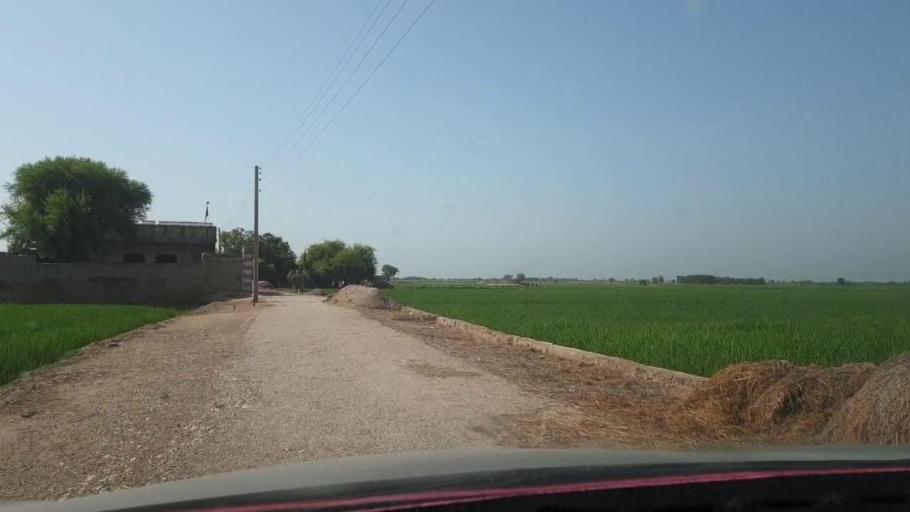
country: PK
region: Sindh
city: Nasirabad
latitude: 27.3823
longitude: 67.8798
